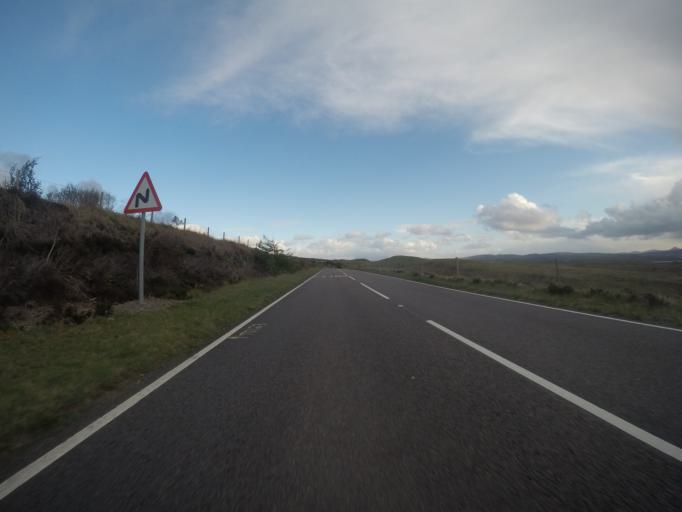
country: GB
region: Scotland
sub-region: Highland
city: Portree
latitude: 57.5505
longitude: -6.3645
